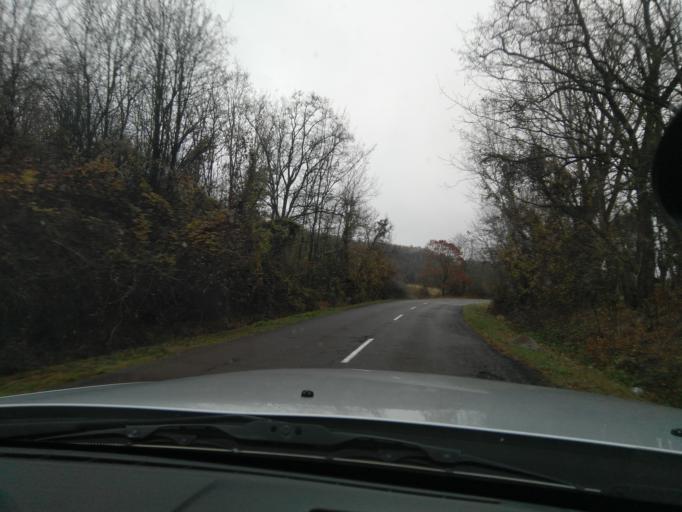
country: HU
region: Nograd
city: Matraterenye
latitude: 48.0468
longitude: 19.9070
